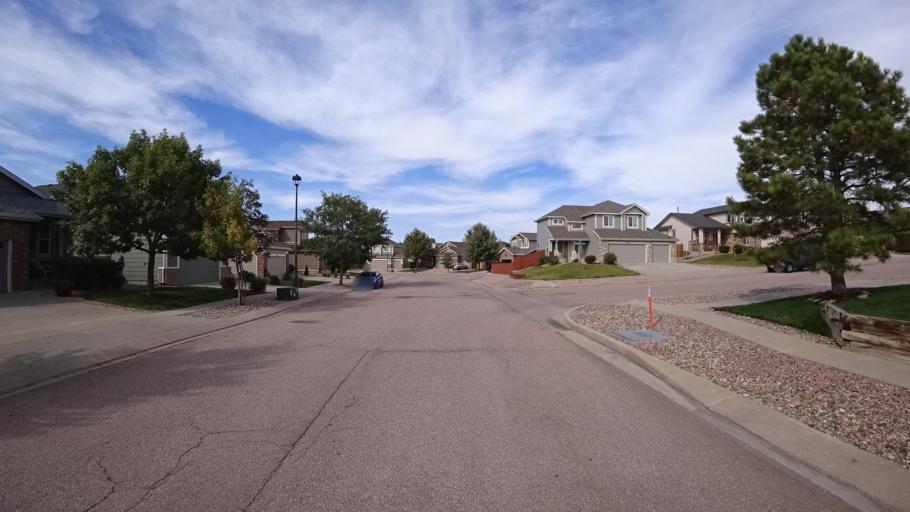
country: US
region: Colorado
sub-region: El Paso County
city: Cimarron Hills
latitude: 38.9105
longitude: -104.6871
